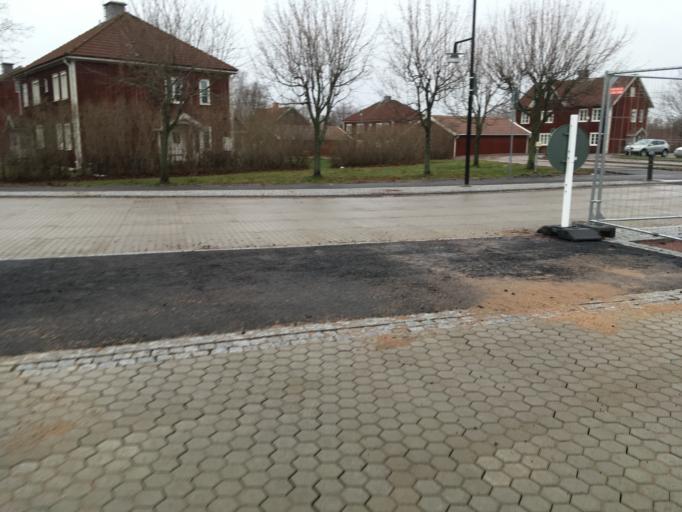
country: SE
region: Vaermland
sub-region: Hammaro Kommun
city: Skoghall
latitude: 59.3234
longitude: 13.4652
